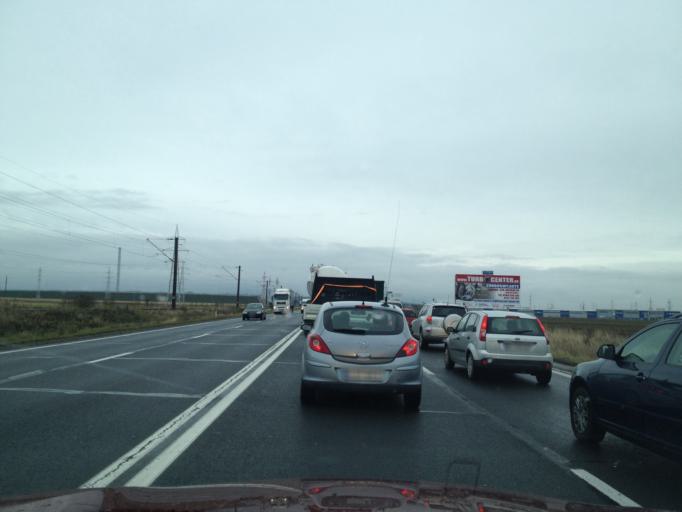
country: RO
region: Brasov
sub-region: Comuna Harman
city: Harman
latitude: 45.6892
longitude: 25.6710
